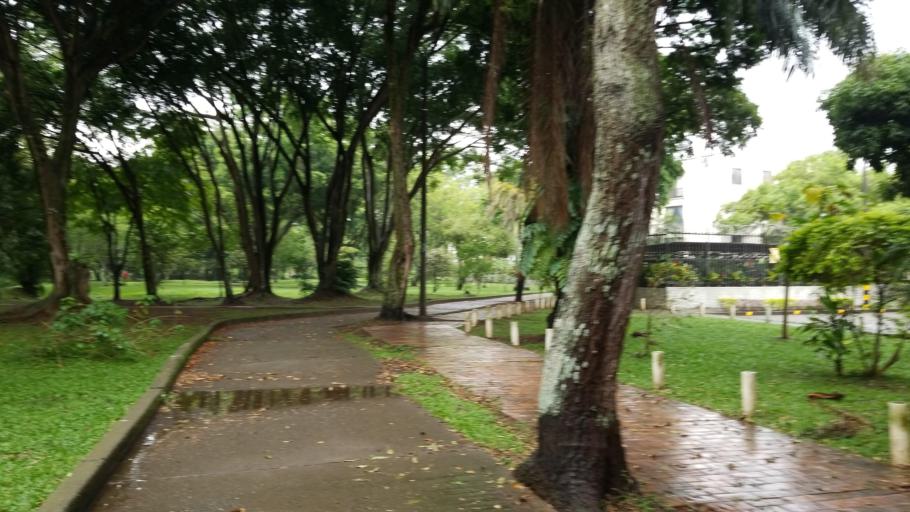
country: CO
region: Valle del Cauca
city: Cali
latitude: 3.3786
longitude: -76.5405
